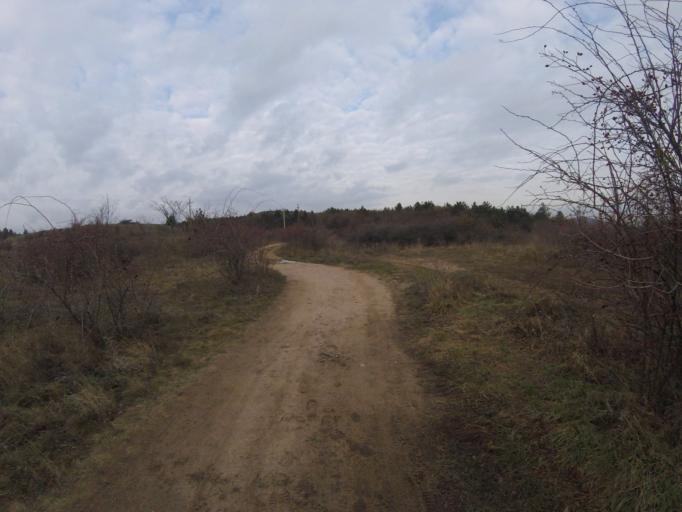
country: HU
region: Fejer
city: Velence
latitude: 47.2500
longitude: 18.6213
